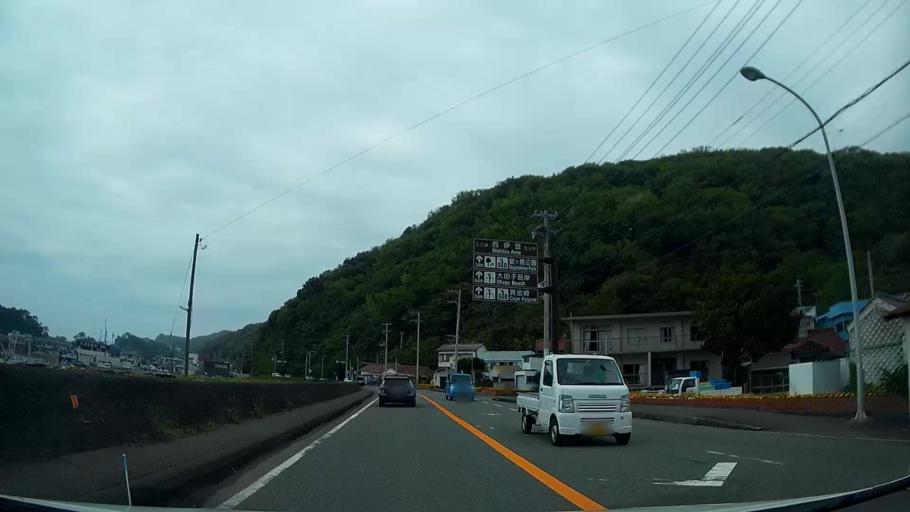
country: JP
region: Shizuoka
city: Heda
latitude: 34.7733
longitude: 138.7713
